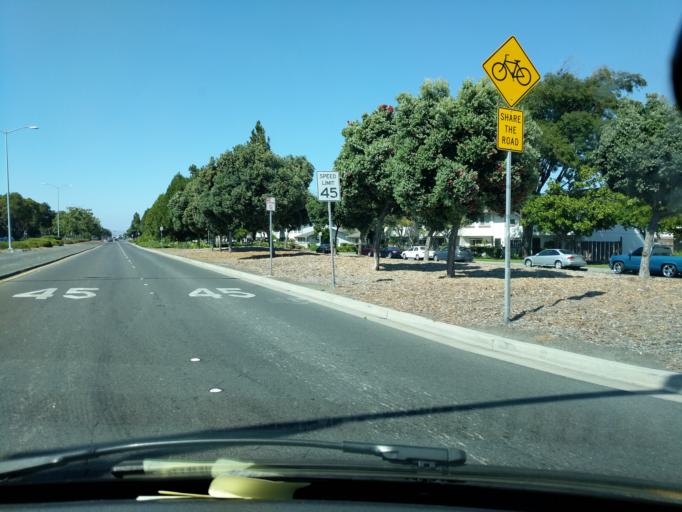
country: US
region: California
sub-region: Alameda County
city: Union City
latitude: 37.5877
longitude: -122.0810
